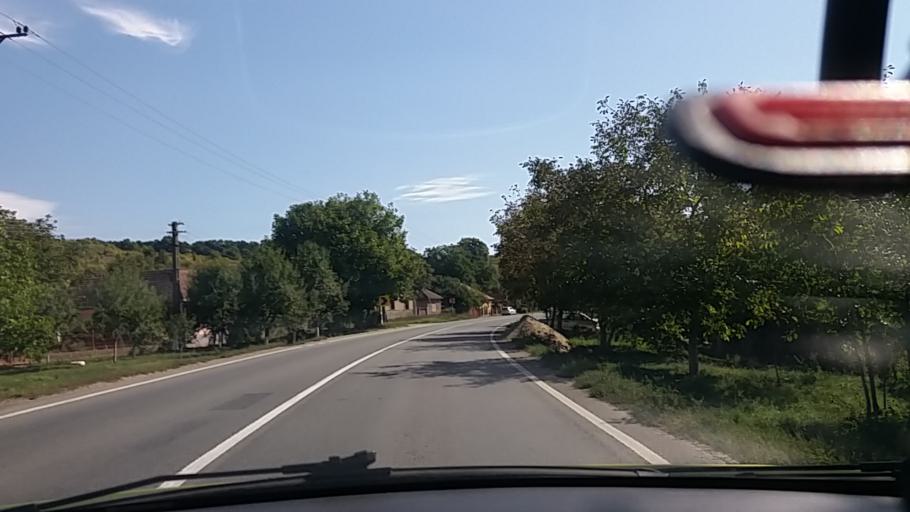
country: RO
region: Arad
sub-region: Comuna Zabrani
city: Neudorf
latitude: 46.1066
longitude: 21.6359
